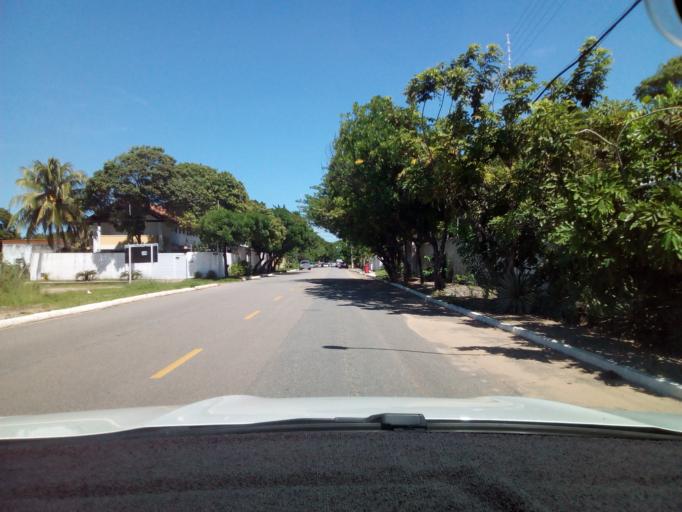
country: BR
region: Paraiba
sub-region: Joao Pessoa
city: Joao Pessoa
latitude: -7.1568
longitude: -34.7959
